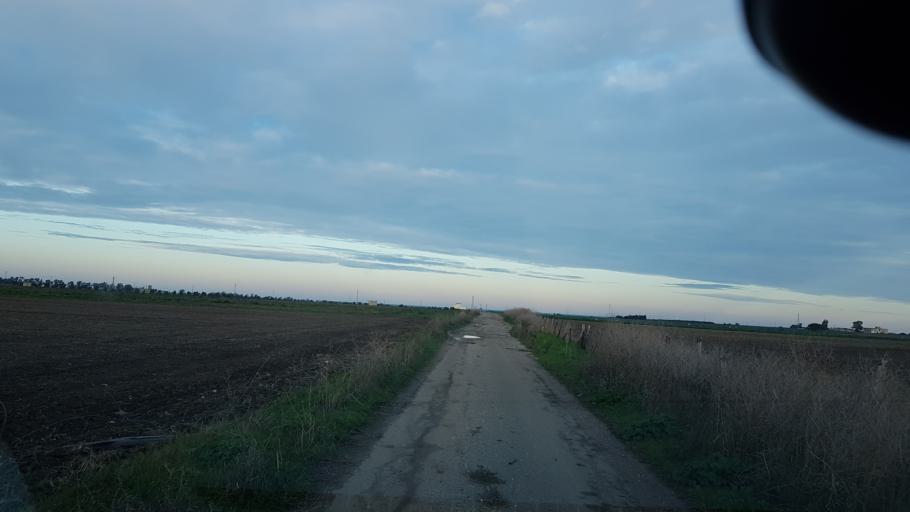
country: IT
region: Apulia
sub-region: Provincia di Brindisi
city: La Rosa
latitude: 40.5982
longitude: 17.9941
